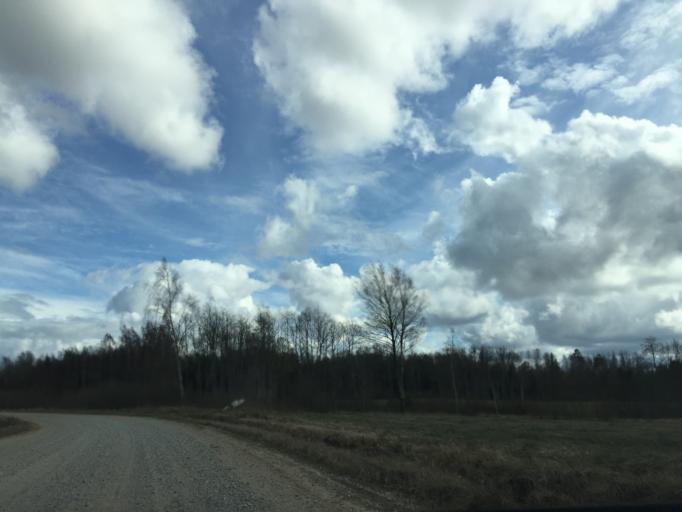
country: LV
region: Limbazu Rajons
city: Limbazi
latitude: 57.6095
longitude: 24.7859
